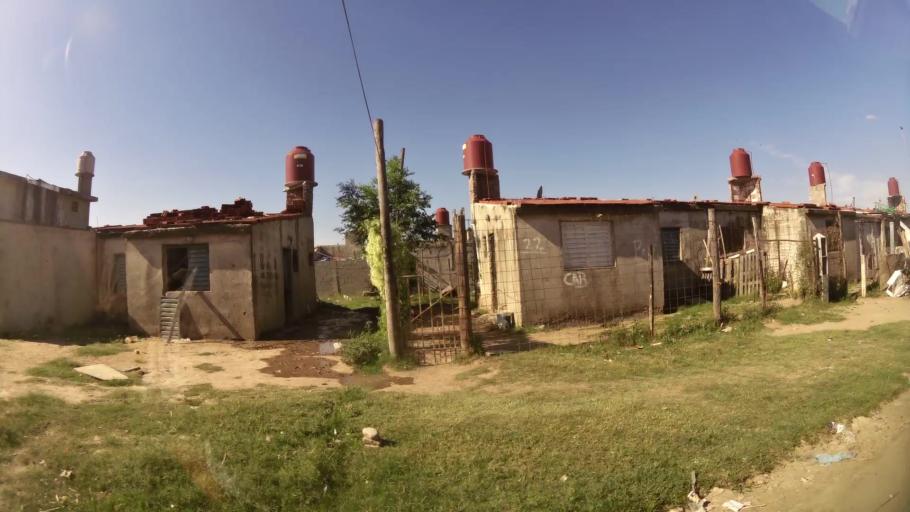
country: AR
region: Cordoba
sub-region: Departamento de Capital
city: Cordoba
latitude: -31.3736
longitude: -64.1914
